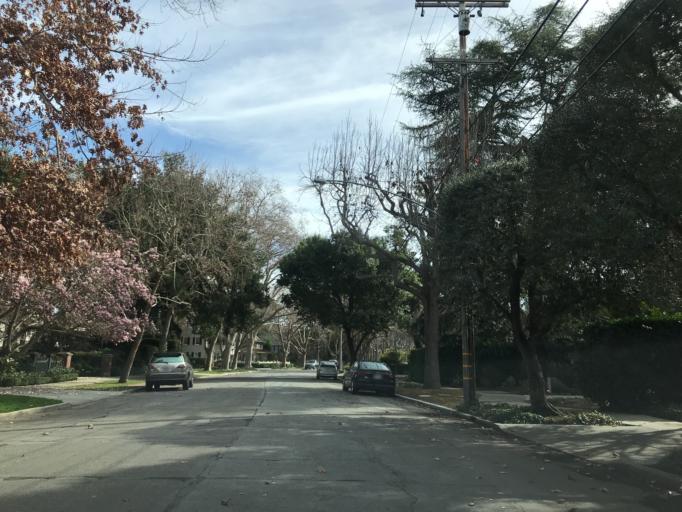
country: US
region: California
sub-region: Santa Clara County
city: Palo Alto
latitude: 37.4346
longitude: -122.1407
